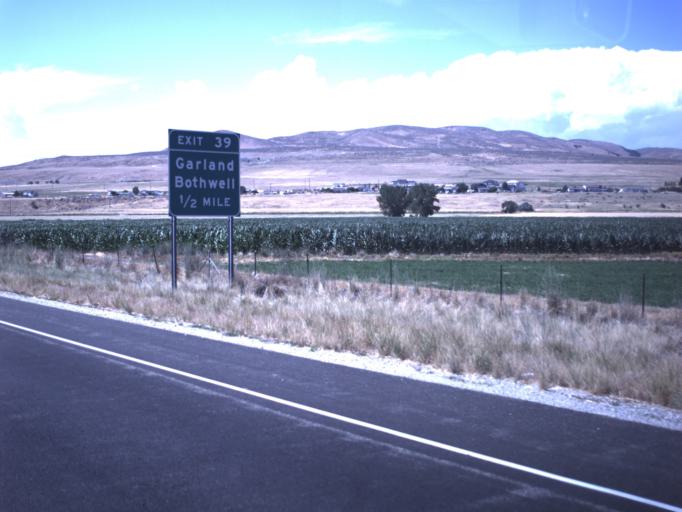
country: US
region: Utah
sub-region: Box Elder County
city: Tremonton
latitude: 41.7142
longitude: -112.2134
